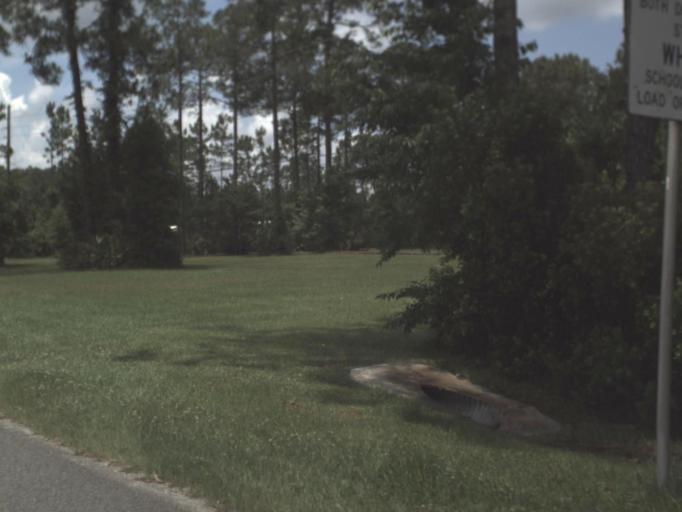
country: US
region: Florida
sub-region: Nassau County
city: Yulee
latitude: 30.6411
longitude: -81.6120
